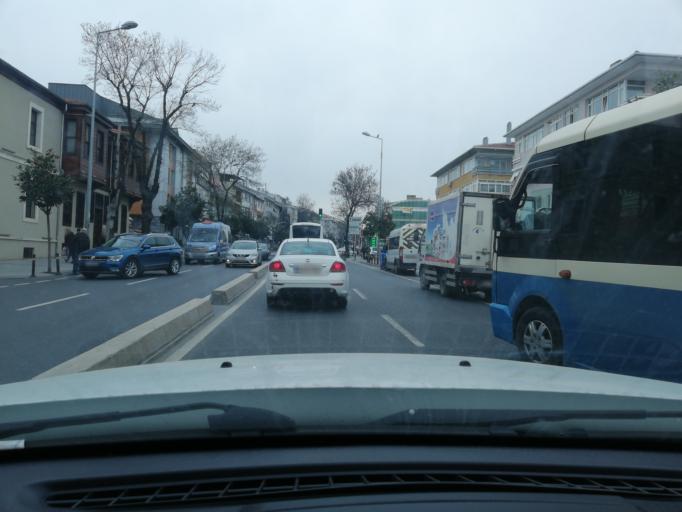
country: TR
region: Istanbul
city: UEskuedar
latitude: 41.0157
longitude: 29.0290
